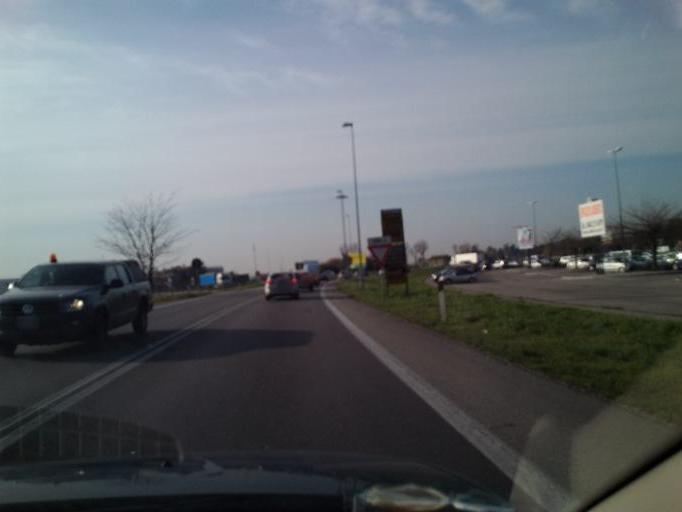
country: IT
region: Veneto
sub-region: Provincia di Verona
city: Dossobuono
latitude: 45.3913
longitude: 10.9021
